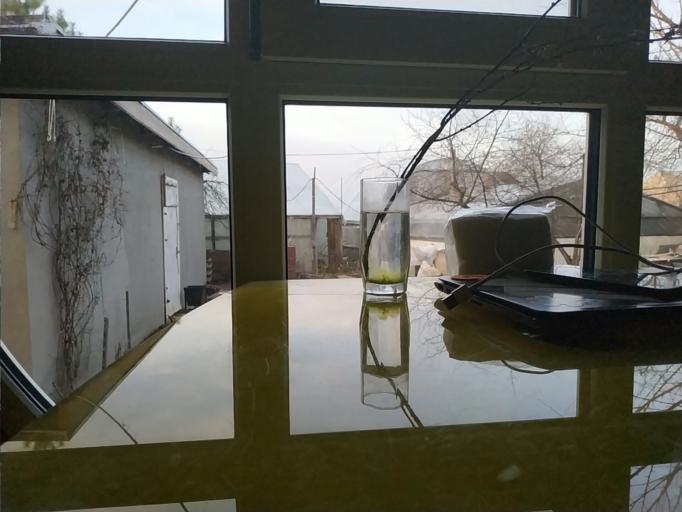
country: RU
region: Republic of Karelia
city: Suoyarvi
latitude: 62.4262
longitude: 32.0149
